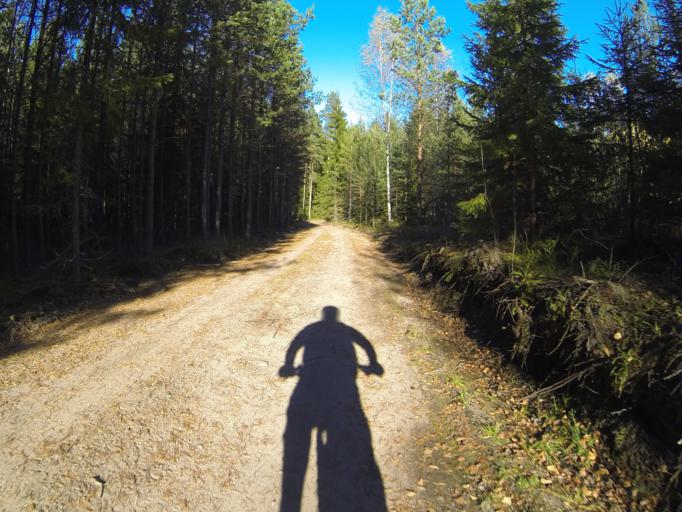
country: FI
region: Varsinais-Suomi
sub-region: Salo
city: Saerkisalo
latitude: 60.2153
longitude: 22.9892
